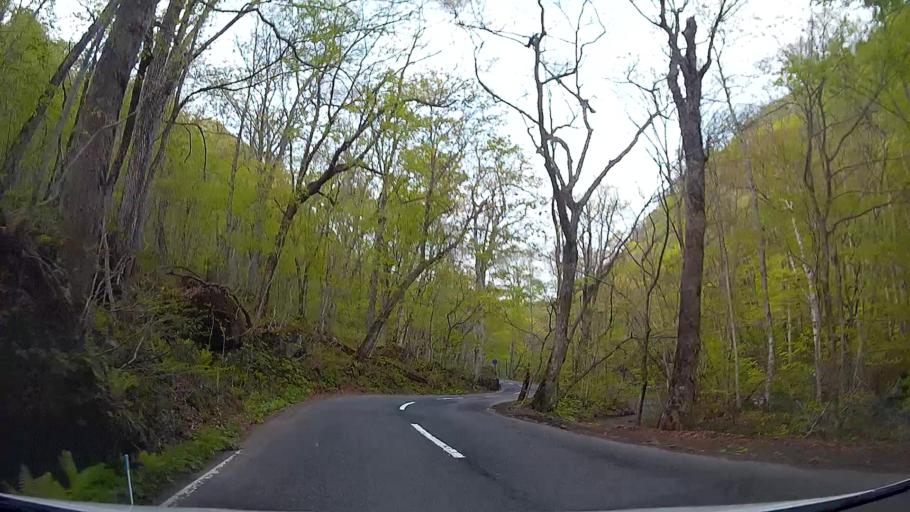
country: JP
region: Aomori
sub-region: Aomori Shi
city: Furudate
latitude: 40.5248
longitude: 140.9741
